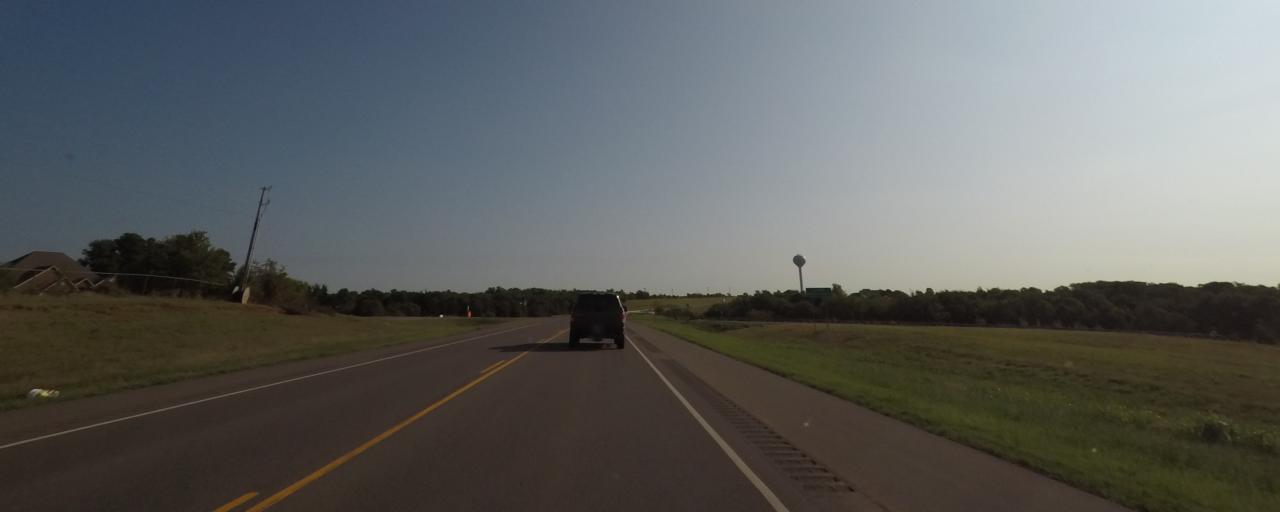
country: US
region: Oklahoma
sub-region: McClain County
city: Blanchard
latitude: 35.1190
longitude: -97.7063
